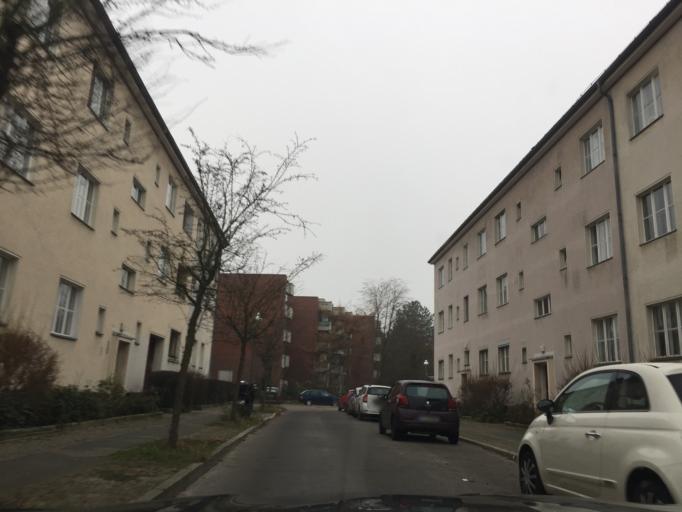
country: DE
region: Berlin
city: Wilhelmstadt
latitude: 52.5185
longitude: 13.1940
